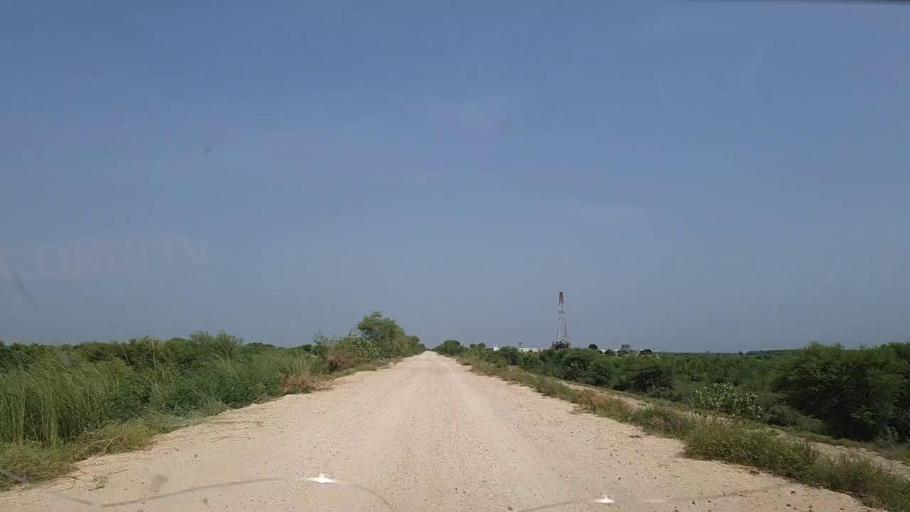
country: PK
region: Sindh
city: Ghotki
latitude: 28.1175
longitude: 69.3815
